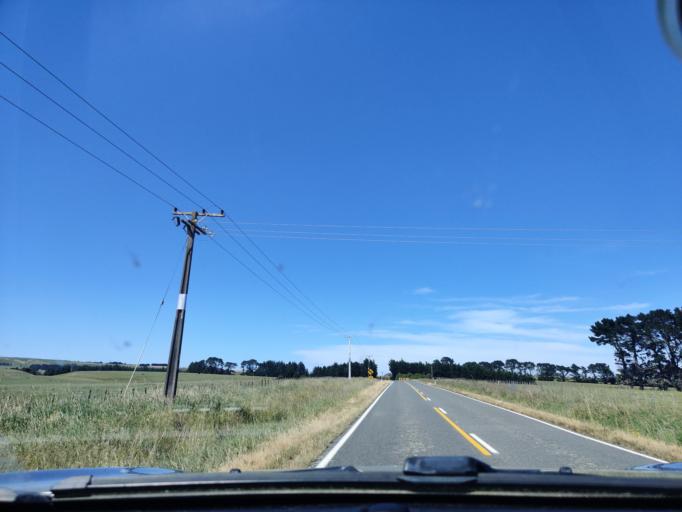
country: NZ
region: Wellington
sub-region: Upper Hutt City
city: Upper Hutt
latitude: -41.3596
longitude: 175.2004
